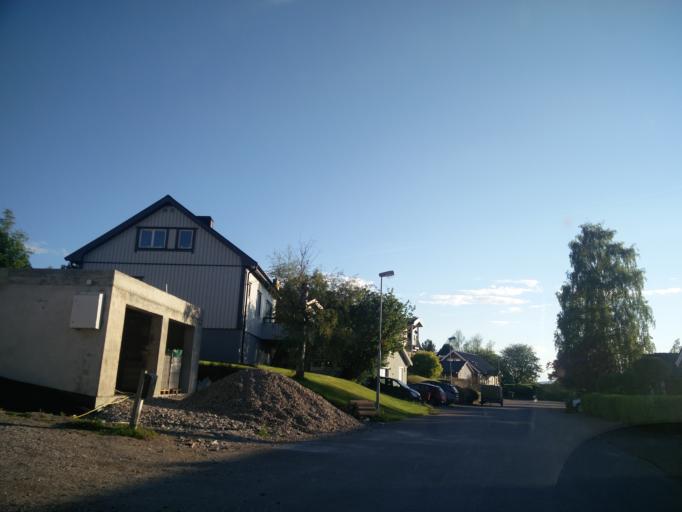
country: SE
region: Vaesternorrland
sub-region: Sundsvalls Kommun
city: Sundsvall
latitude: 62.4058
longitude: 17.2812
